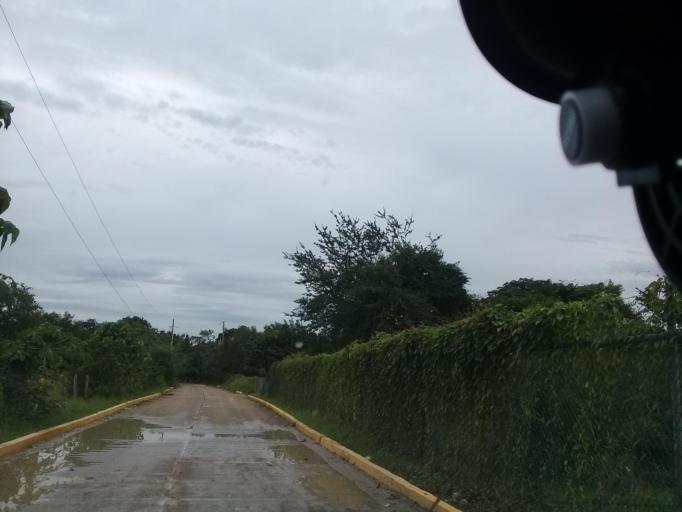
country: MX
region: Hidalgo
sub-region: Huejutla de Reyes
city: Chalahuiyapa
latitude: 21.1635
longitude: -98.3644
